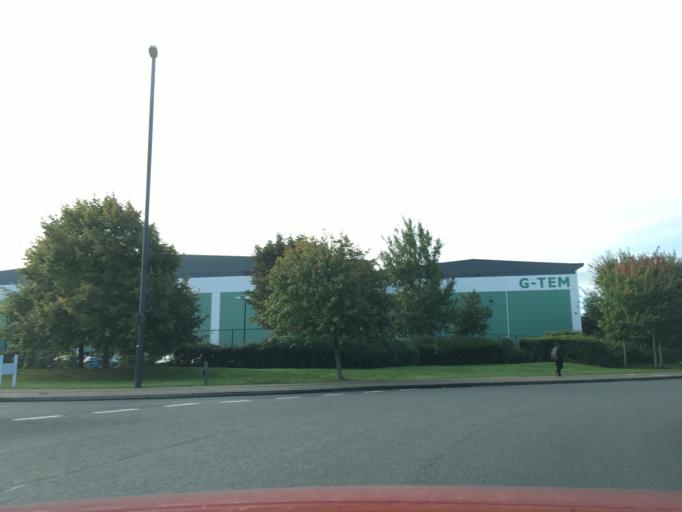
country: GB
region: England
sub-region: Gloucestershire
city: Churchdown
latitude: 51.8466
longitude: -2.1719
